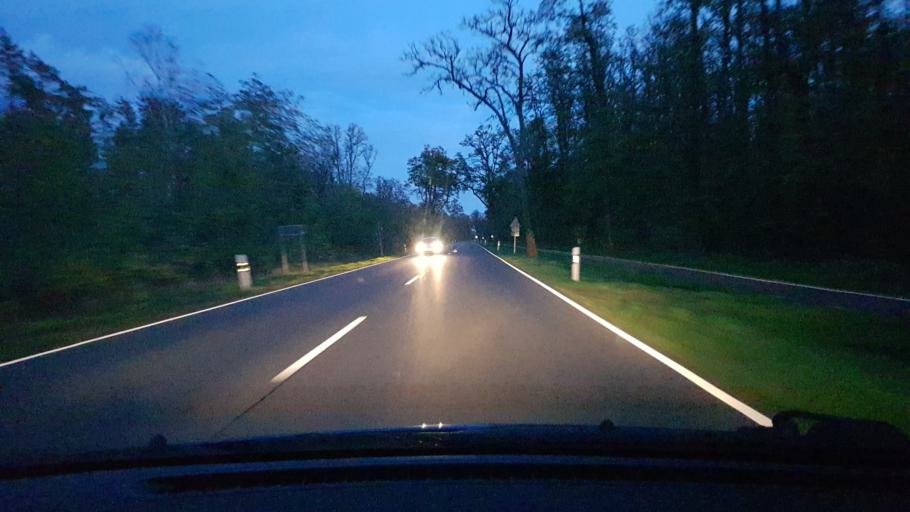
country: DE
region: Saxony-Anhalt
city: Rodleben
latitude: 51.9230
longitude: 12.1633
